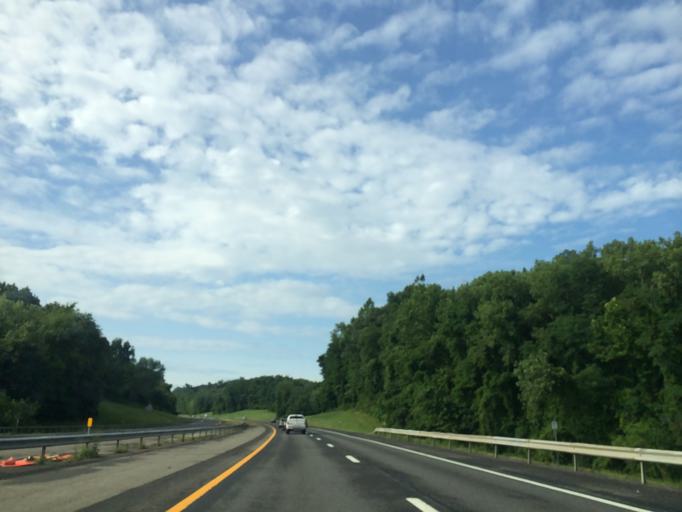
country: US
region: New York
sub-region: Ulster County
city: Rosendale Village
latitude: 41.8515
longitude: -74.0597
